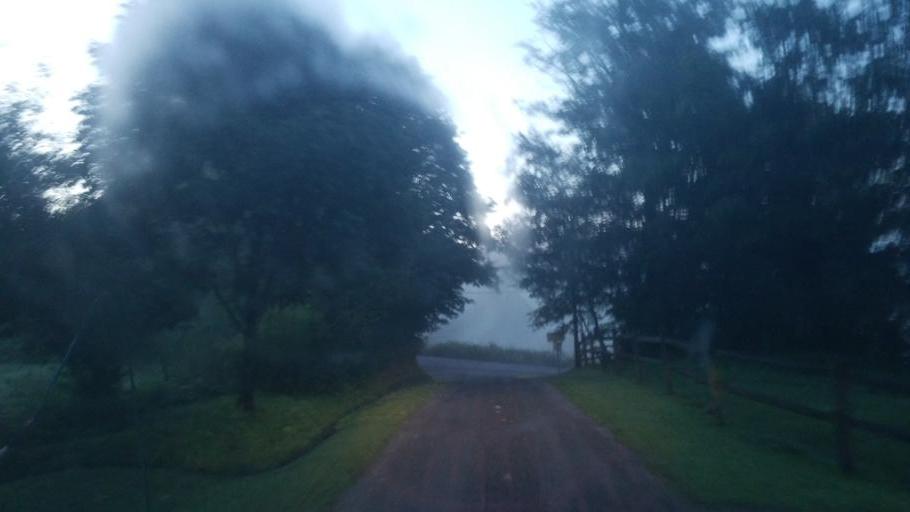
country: US
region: New York
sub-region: Allegany County
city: Andover
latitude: 41.9285
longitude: -77.7856
